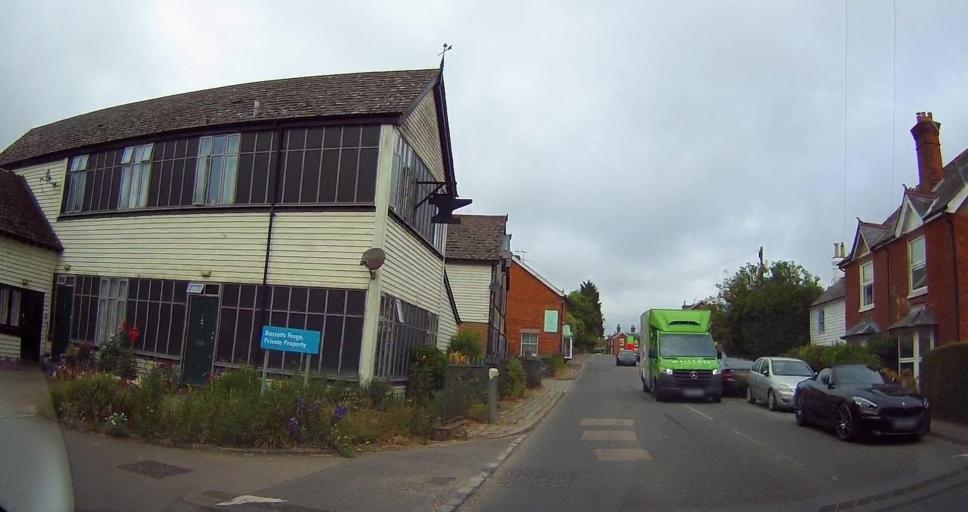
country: GB
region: England
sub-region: East Sussex
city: Wadhurst
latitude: 51.0657
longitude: 0.3296
